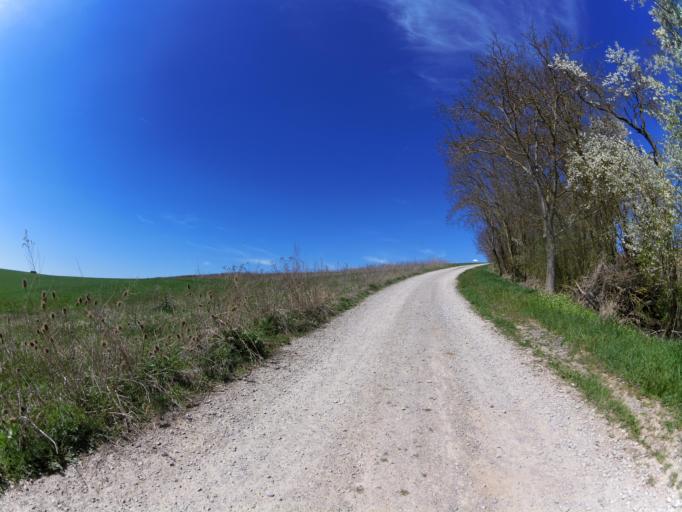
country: DE
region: Bavaria
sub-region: Regierungsbezirk Unterfranken
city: Winterhausen
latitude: 49.6932
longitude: 9.9884
